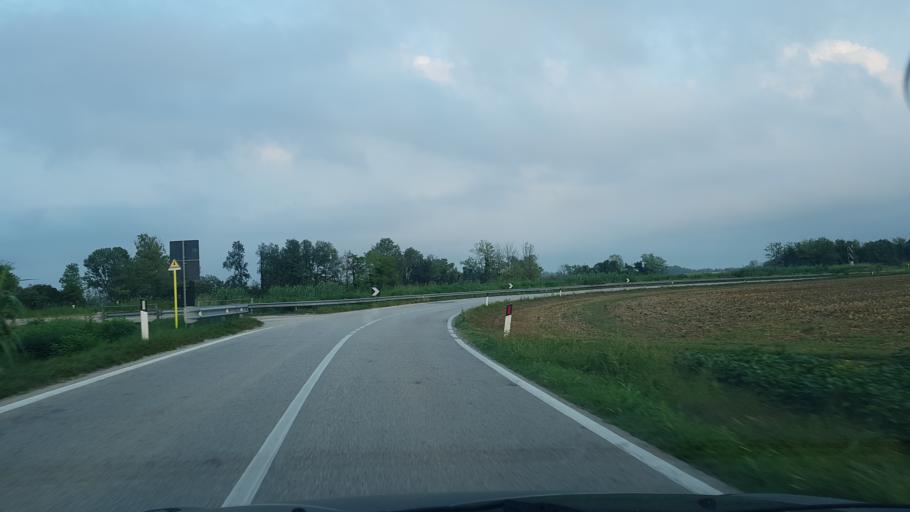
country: IT
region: Friuli Venezia Giulia
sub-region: Provincia di Udine
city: Trivignano Udinese
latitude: 45.9374
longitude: 13.3633
